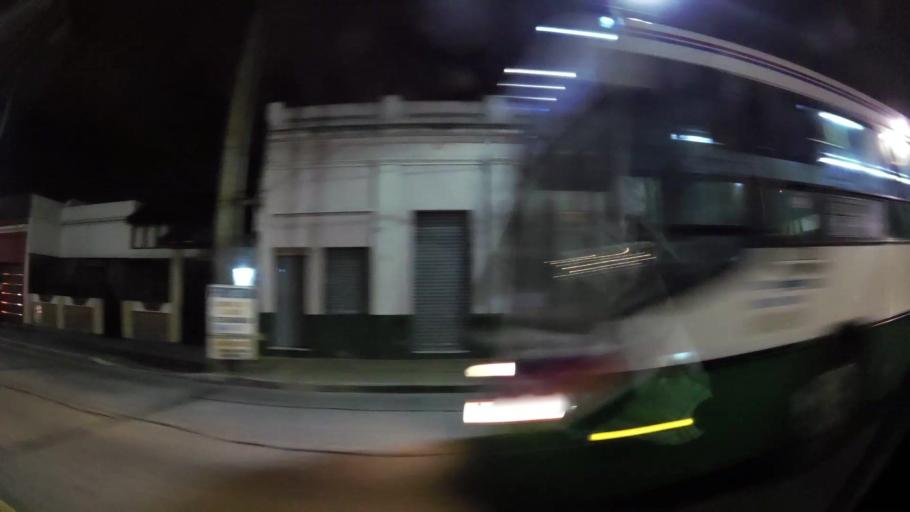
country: AR
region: Buenos Aires
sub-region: Partido de Avellaneda
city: Avellaneda
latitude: -34.6867
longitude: -58.3439
